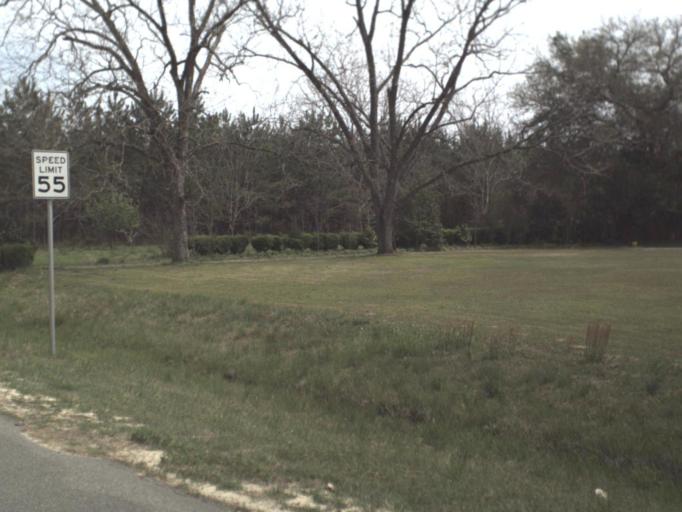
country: US
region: Alabama
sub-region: Geneva County
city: Geneva
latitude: 30.9323
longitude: -85.9653
